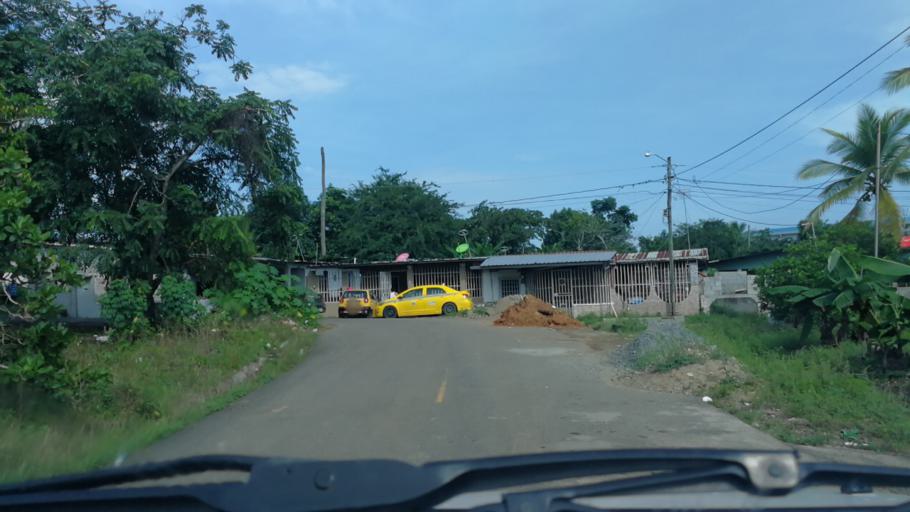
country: PA
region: Panama
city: Pacora
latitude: 9.0844
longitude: -79.2940
